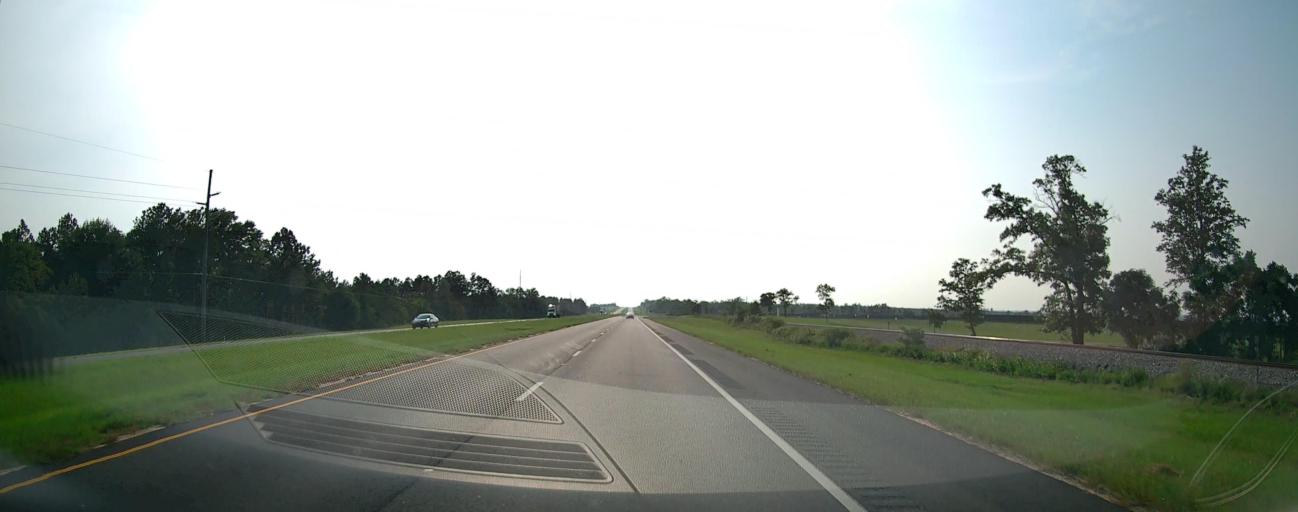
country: US
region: Georgia
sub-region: Taylor County
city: Butler
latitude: 32.5735
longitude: -84.2953
